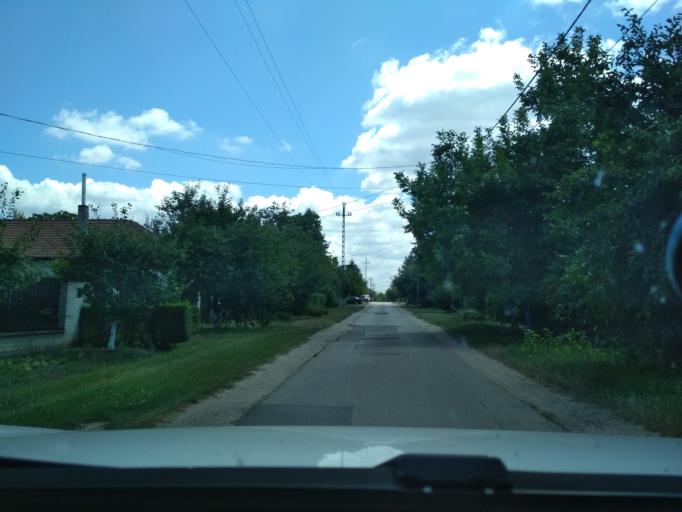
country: HU
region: Fejer
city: Kapolnasnyek
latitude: 47.2207
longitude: 18.6693
